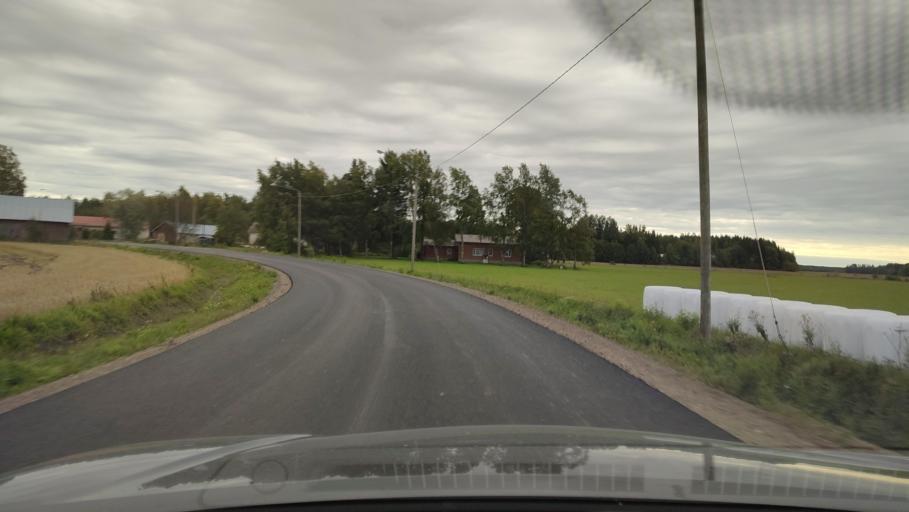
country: FI
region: Southern Ostrobothnia
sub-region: Suupohja
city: Karijoki
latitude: 62.2374
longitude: 21.5683
